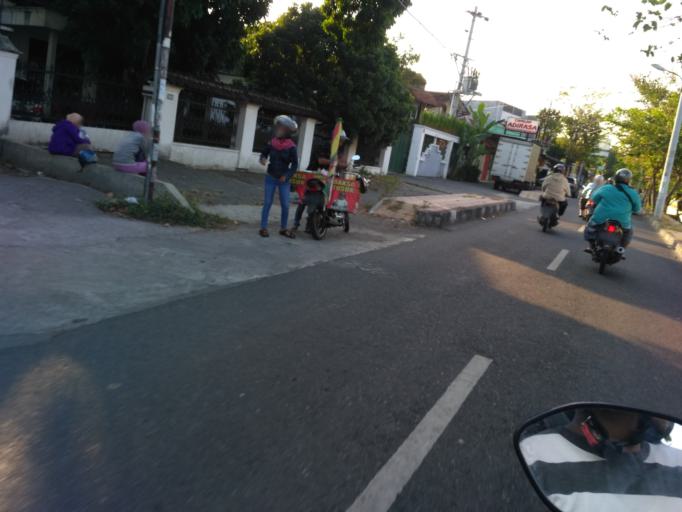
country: ID
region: Daerah Istimewa Yogyakarta
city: Yogyakarta
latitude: -7.8141
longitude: 110.3832
